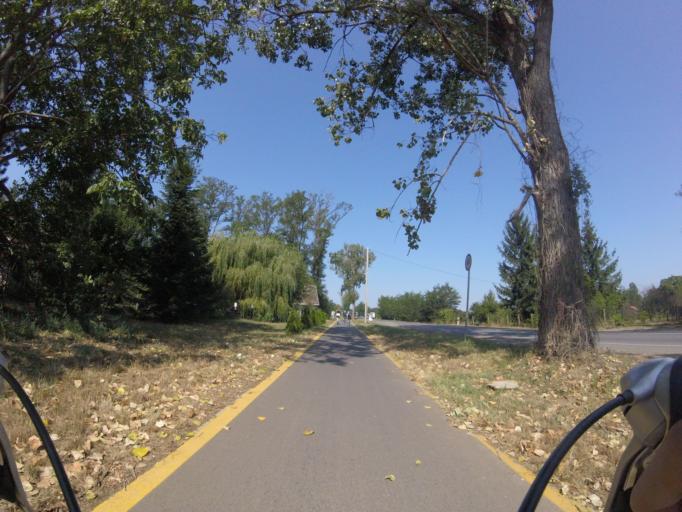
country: HU
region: Szabolcs-Szatmar-Bereg
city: Nyirtelek
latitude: 47.9878
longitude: 21.6693
